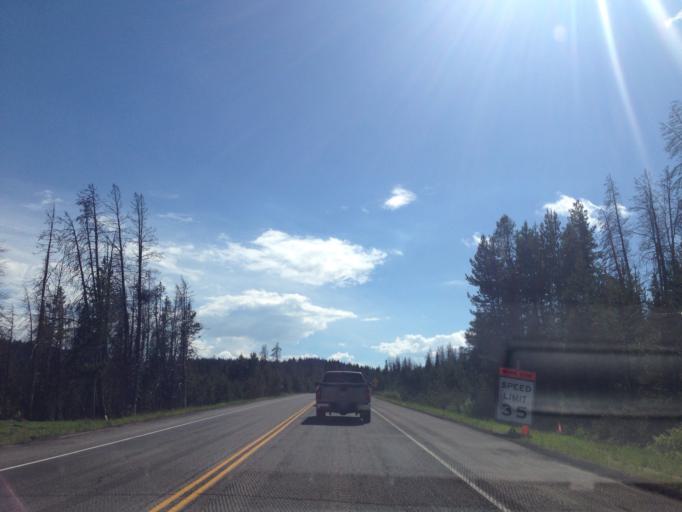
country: US
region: Colorado
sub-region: Routt County
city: Steamboat Springs
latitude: 40.3779
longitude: -106.7202
